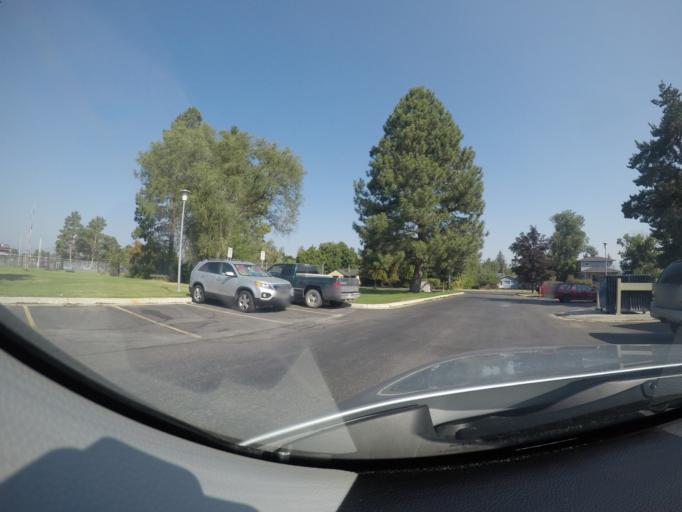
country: US
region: Montana
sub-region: Missoula County
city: Missoula
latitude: 46.8483
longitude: -113.9933
